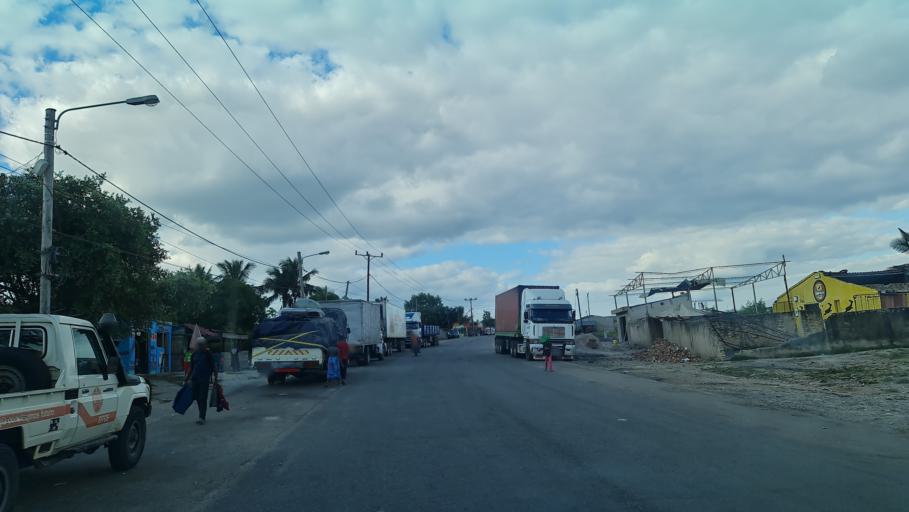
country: MZ
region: Manica
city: Chimoio
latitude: -19.2106
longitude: 33.9260
